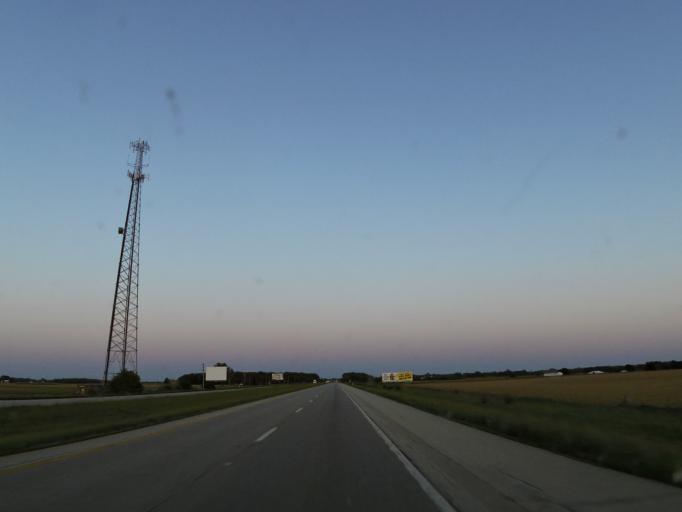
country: US
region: Indiana
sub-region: Montgomery County
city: Crawfordsville
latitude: 40.0212
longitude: -86.7782
